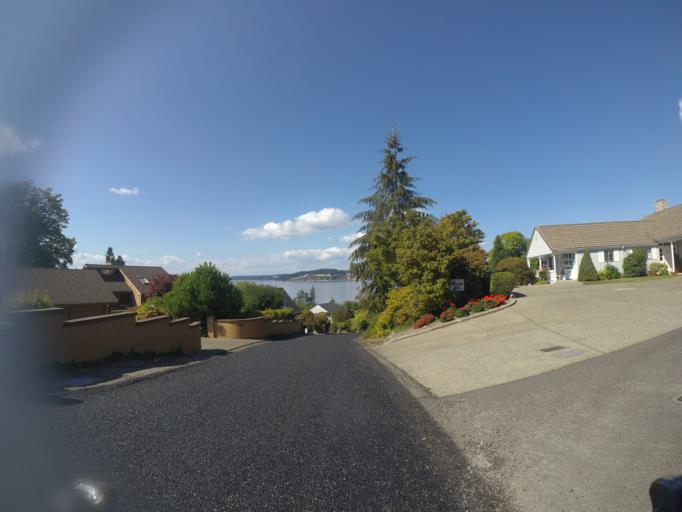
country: US
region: Washington
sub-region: Pierce County
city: University Place
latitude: 47.2341
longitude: -122.5619
